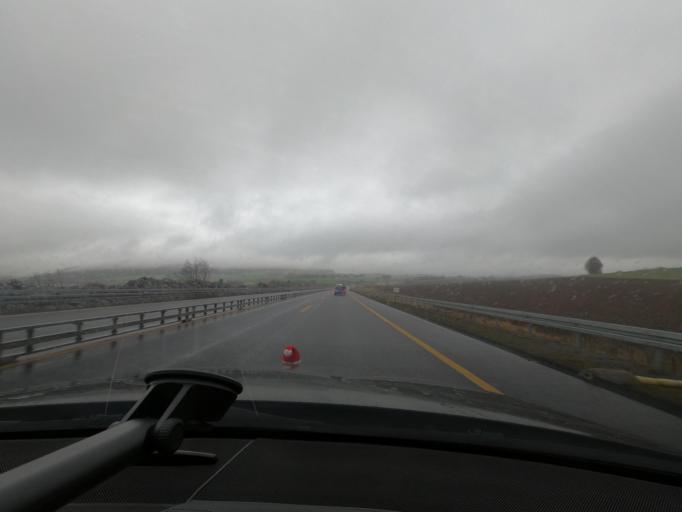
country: DE
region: Lower Saxony
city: Kalefeld
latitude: 51.7834
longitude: 10.0380
